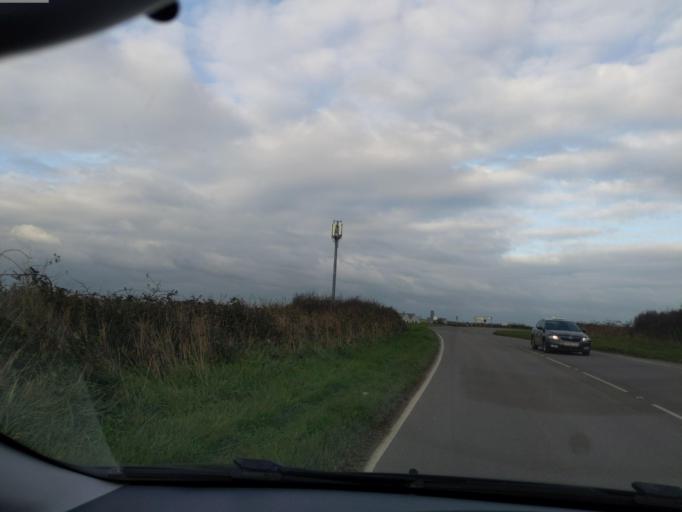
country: GB
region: England
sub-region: Cornwall
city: Padstow
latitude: 50.5325
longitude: -4.9510
